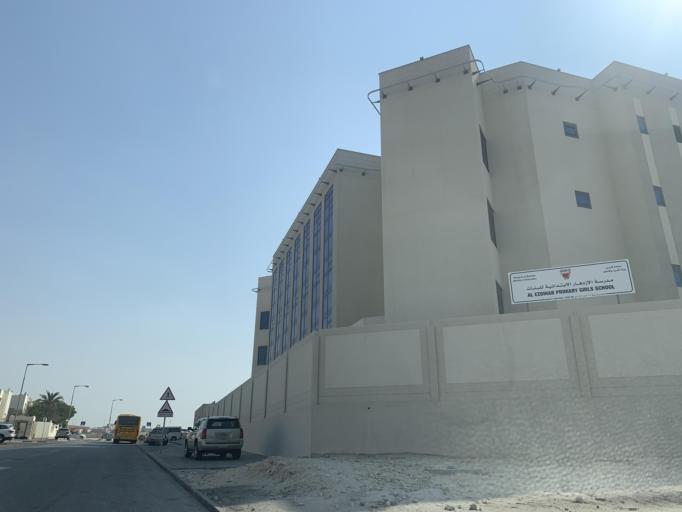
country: BH
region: Central Governorate
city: Madinat Hamad
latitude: 26.1248
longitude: 50.4953
